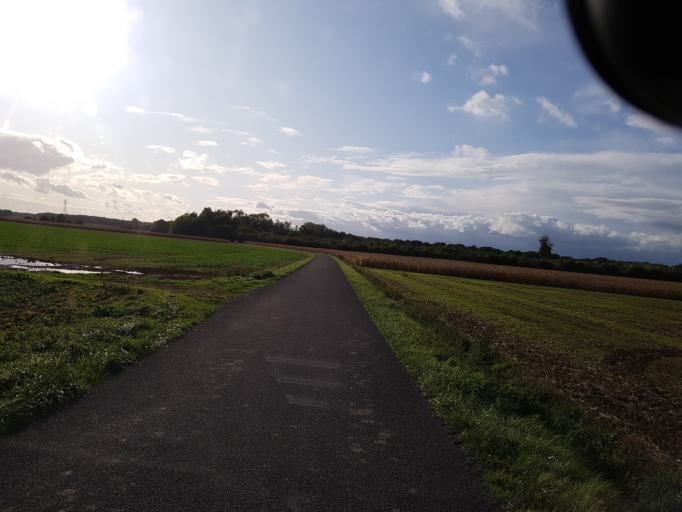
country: FR
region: Ile-de-France
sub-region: Departement de Seine-et-Marne
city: Touquin
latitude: 48.7500
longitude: 3.0253
